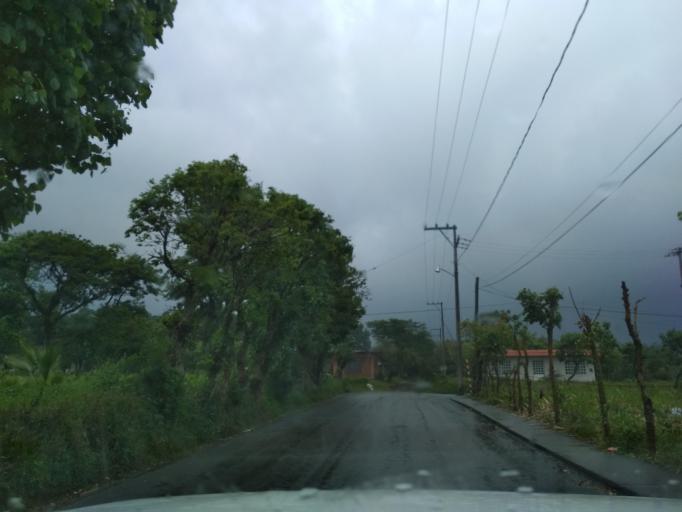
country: MX
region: Veracruz
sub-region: Mariano Escobedo
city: Chicola
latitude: 18.9008
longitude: -97.1187
